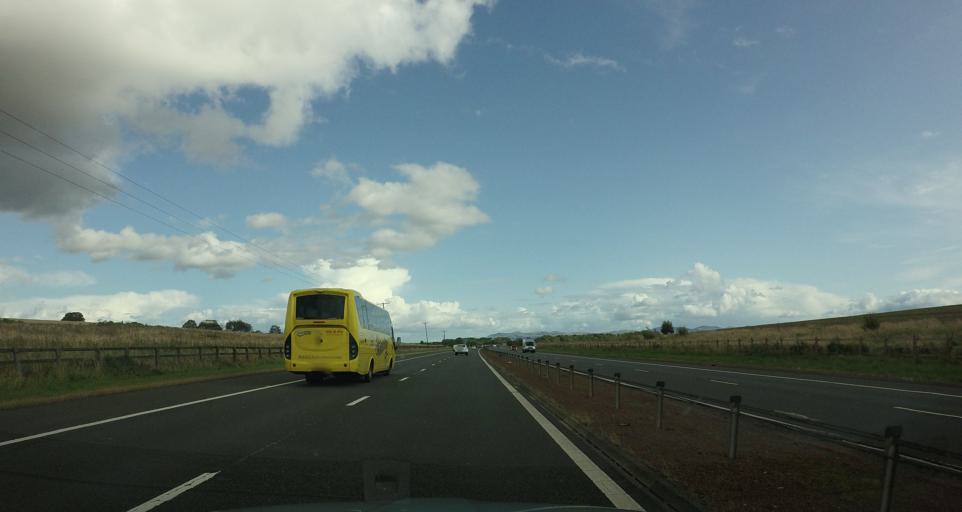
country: GB
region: Scotland
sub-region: West Lothian
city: Broxburn
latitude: 55.9728
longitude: -3.4645
